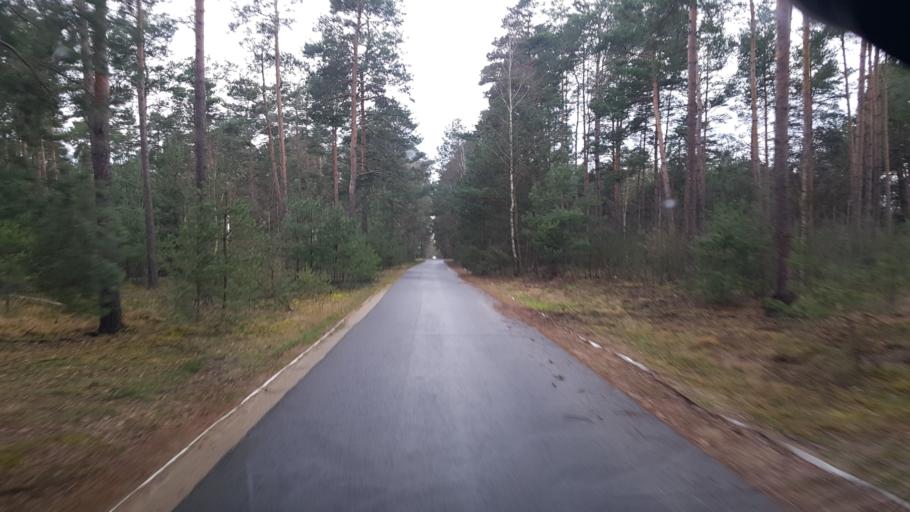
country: DE
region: Brandenburg
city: Crinitz
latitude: 51.6638
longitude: 13.8006
